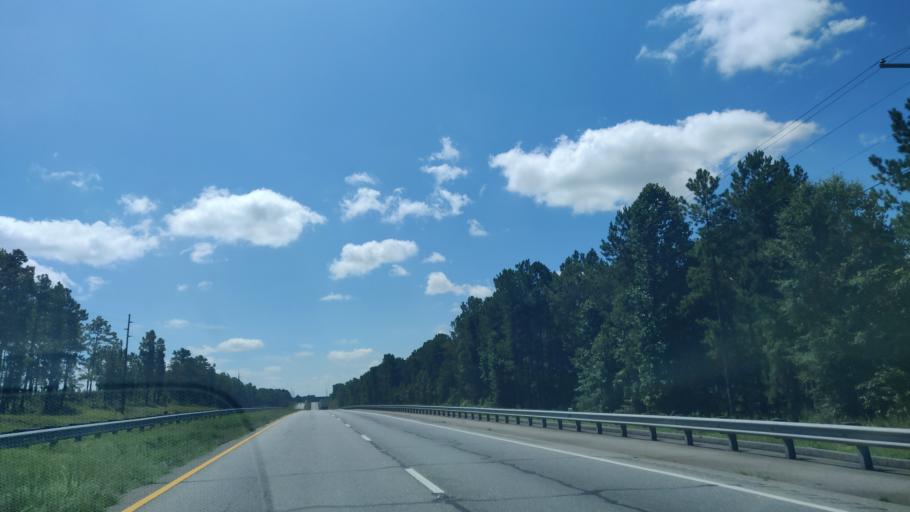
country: US
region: Georgia
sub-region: Muscogee County
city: Columbus
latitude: 32.3883
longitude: -84.8785
